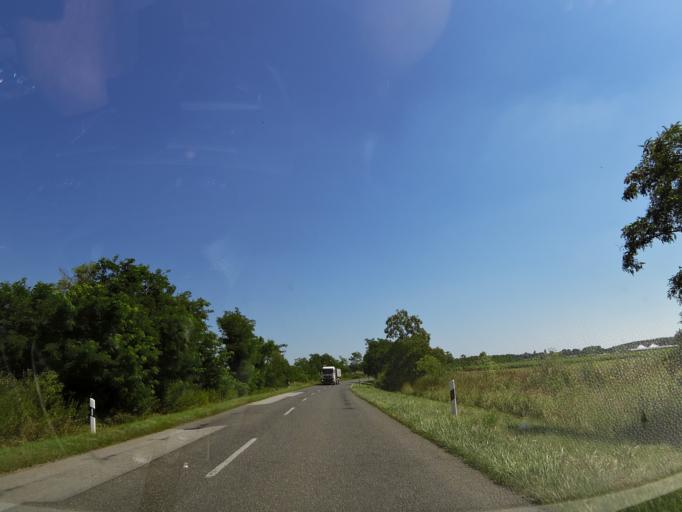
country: HU
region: Jasz-Nagykun-Szolnok
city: Kunhegyes
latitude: 47.3032
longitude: 20.6031
